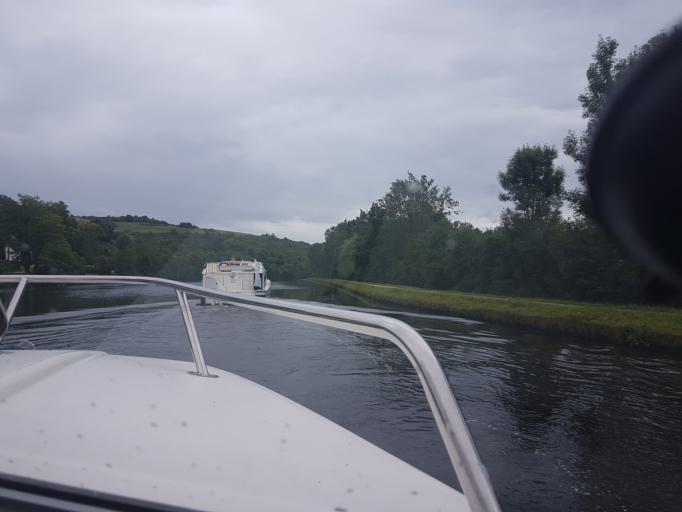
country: FR
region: Bourgogne
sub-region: Departement de l'Yonne
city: Champs-sur-Yonne
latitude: 47.7227
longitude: 3.6245
